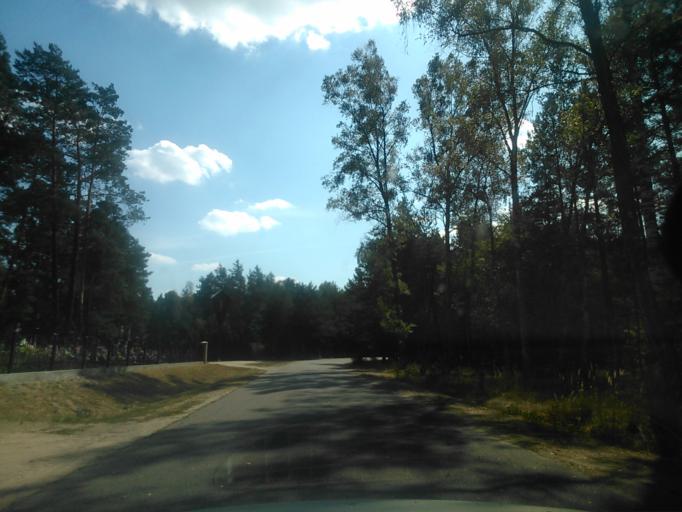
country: PL
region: Masovian Voivodeship
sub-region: Powiat ostrolecki
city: Czarnia
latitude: 53.3527
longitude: 21.2081
